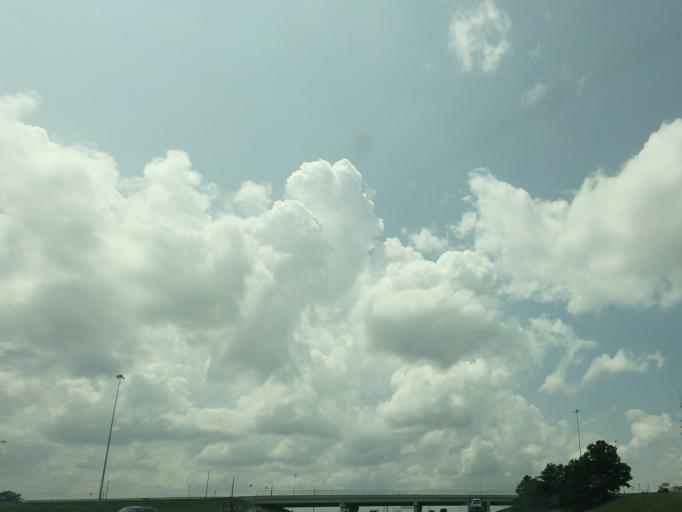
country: US
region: Georgia
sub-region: Bibb County
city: West Point
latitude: 32.7462
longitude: -83.7178
